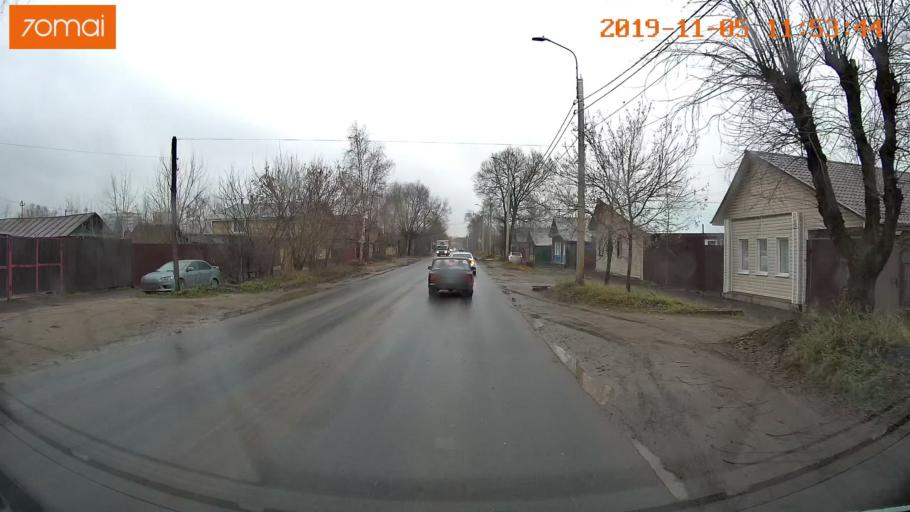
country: RU
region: Ivanovo
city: Bogorodskoye
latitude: 56.9947
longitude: 41.0305
